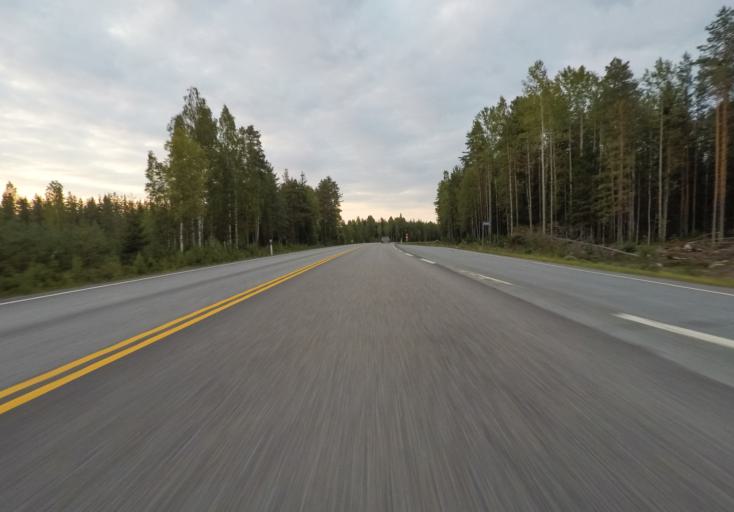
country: FI
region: Central Finland
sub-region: Jyvaeskylae
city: Hankasalmi
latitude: 62.3634
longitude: 26.5727
